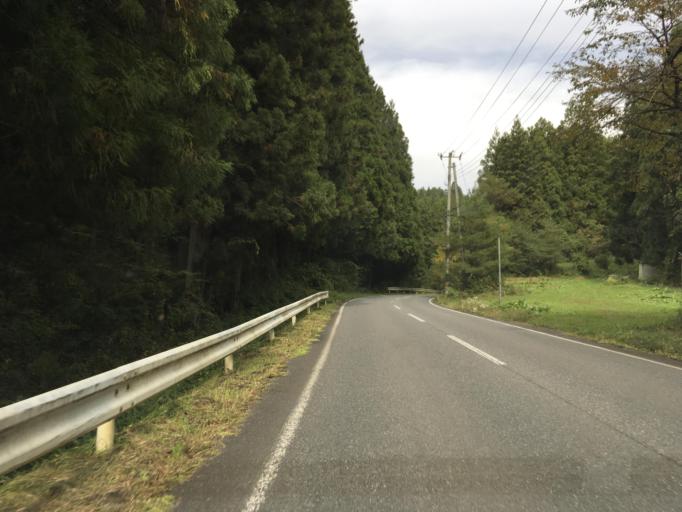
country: JP
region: Iwate
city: Mizusawa
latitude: 39.0383
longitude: 141.3015
